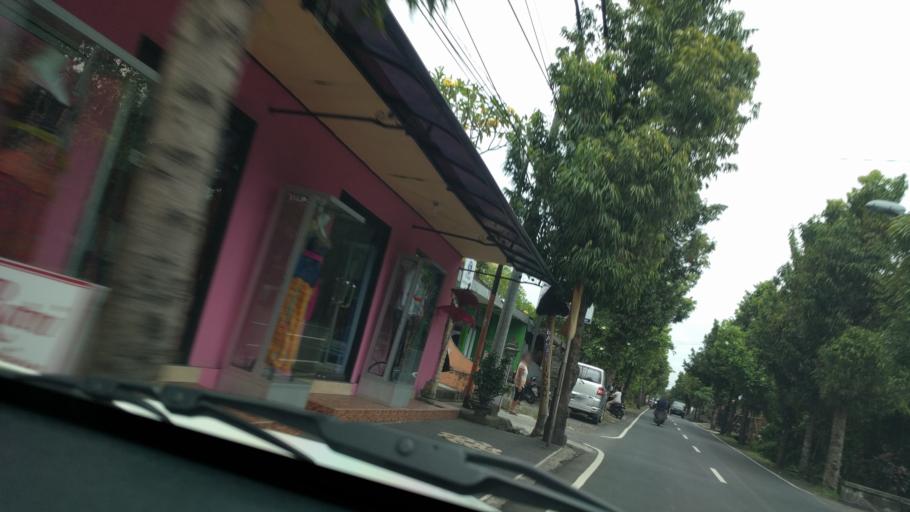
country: ID
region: Bali
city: Banjar Pande
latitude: -8.5128
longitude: 115.2407
